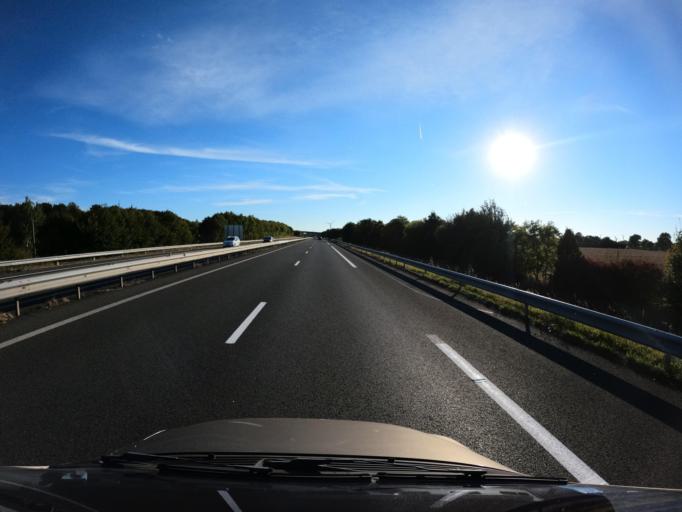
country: FR
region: Pays de la Loire
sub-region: Departement de Maine-et-Loire
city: Chemille-Melay
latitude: 47.2041
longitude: -0.7694
